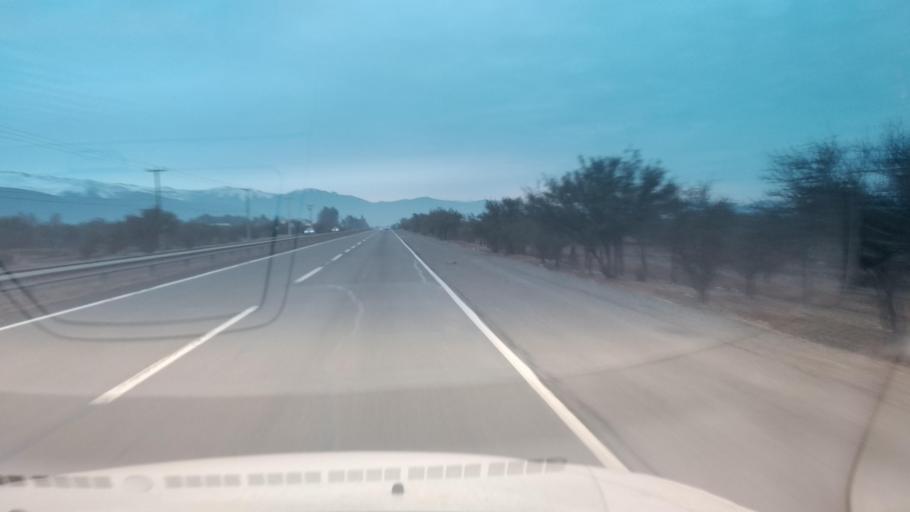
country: CL
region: Santiago Metropolitan
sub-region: Provincia de Chacabuco
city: Chicureo Abajo
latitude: -33.1321
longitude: -70.6694
